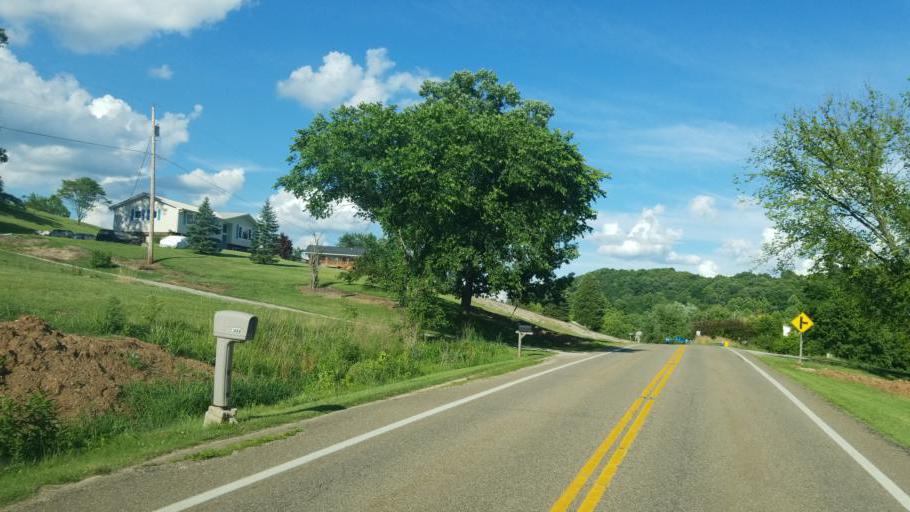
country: US
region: Ohio
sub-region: Gallia County
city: Gallipolis
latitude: 38.7949
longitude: -82.2794
